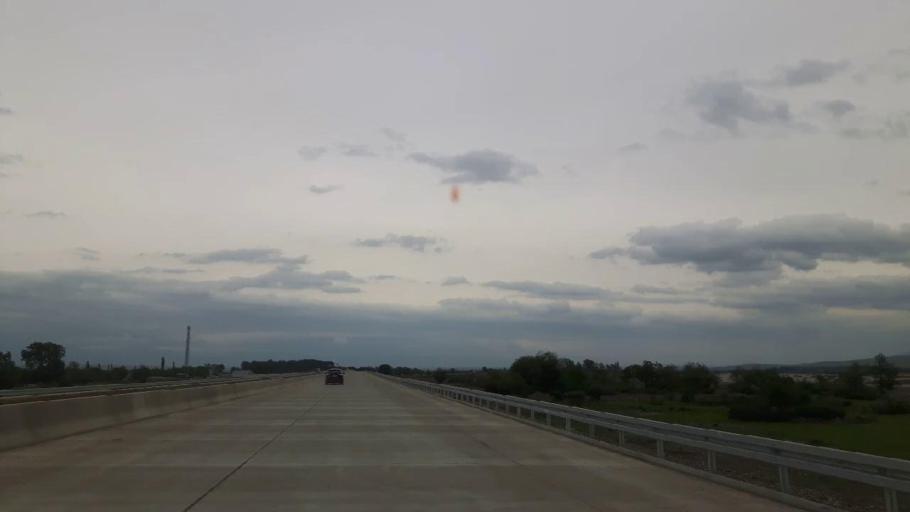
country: GE
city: Agara
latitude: 42.0218
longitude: 43.7492
